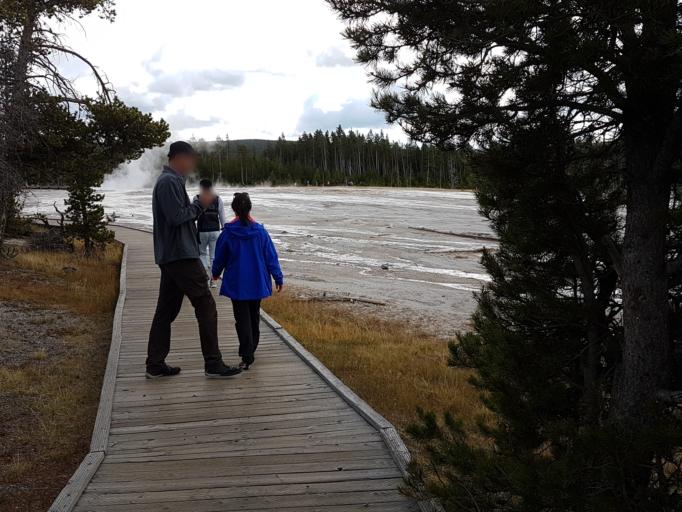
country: US
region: Montana
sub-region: Gallatin County
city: West Yellowstone
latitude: 44.5501
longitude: -110.8082
